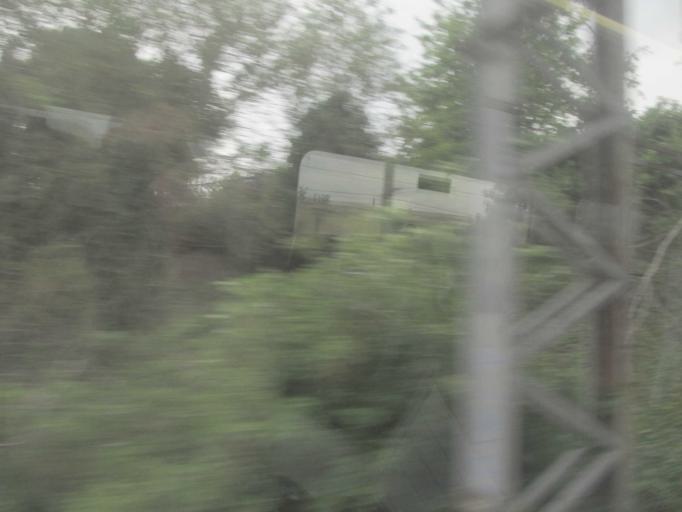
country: GB
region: England
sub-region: Bedford
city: Bedford
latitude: 52.1252
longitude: -0.4778
